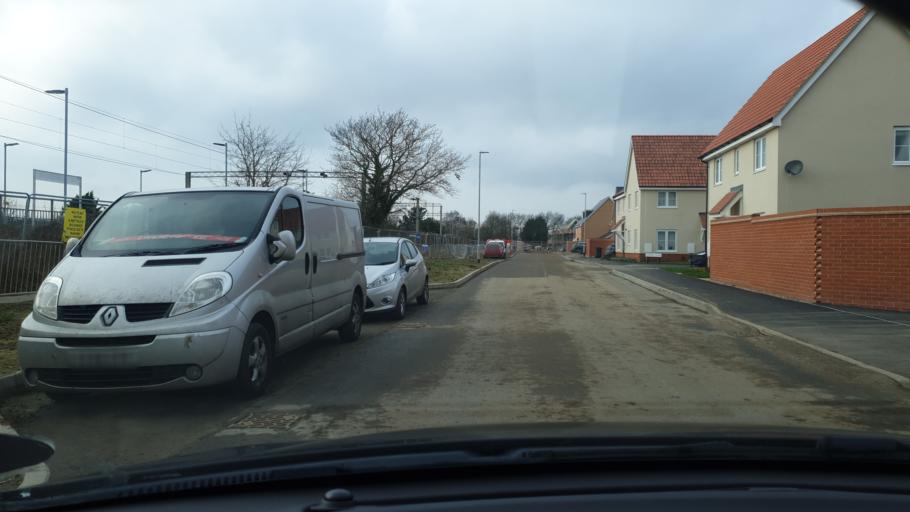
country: GB
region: England
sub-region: Essex
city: Alresford
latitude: 51.8542
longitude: 0.9956
